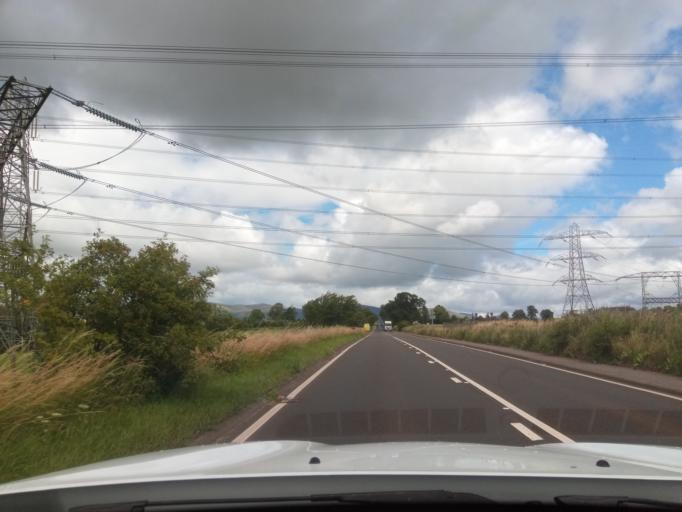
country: GB
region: Scotland
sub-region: Fife
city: Kincardine
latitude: 56.0874
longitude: -3.7194
